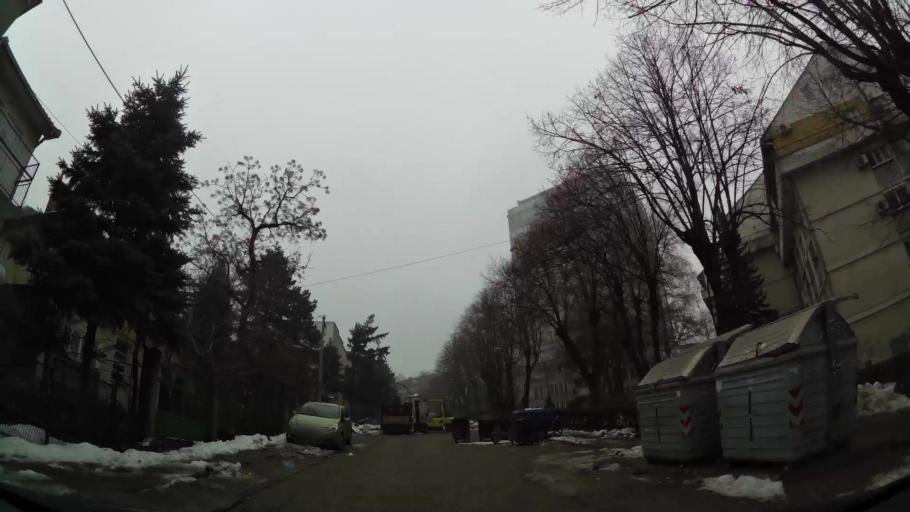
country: RS
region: Central Serbia
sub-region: Belgrade
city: Cukarica
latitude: 44.7783
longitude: 20.4211
